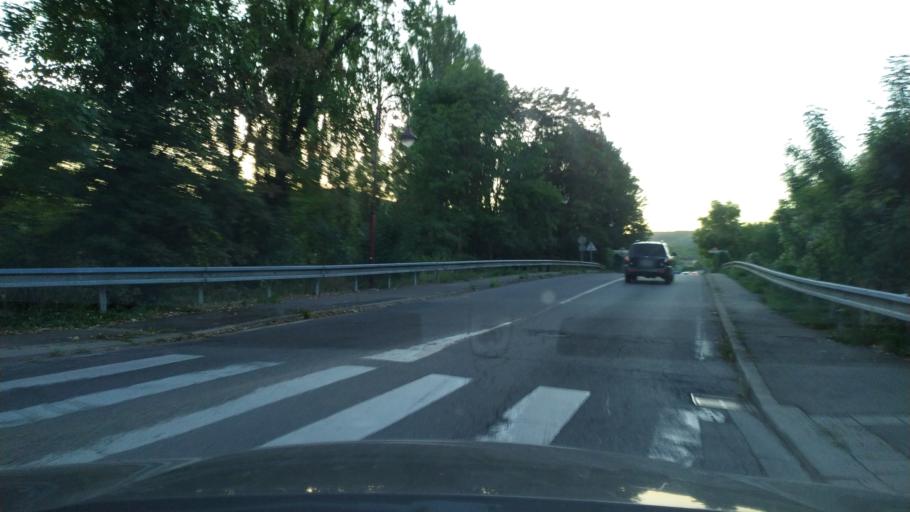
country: FR
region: Lorraine
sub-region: Departement de la Moselle
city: Jouy-aux-Arches
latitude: 49.0690
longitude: 6.0833
